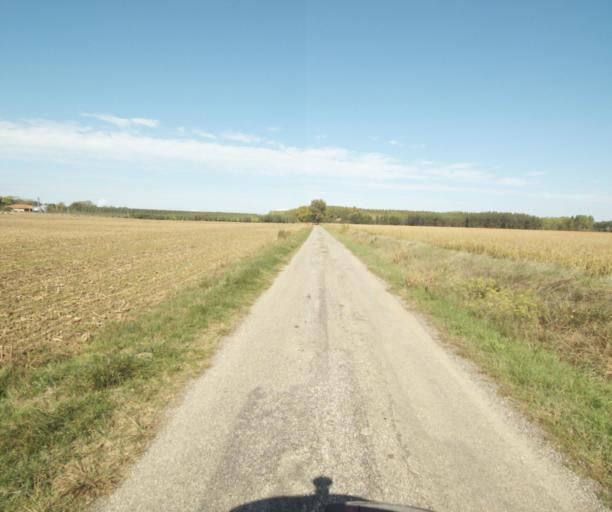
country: FR
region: Midi-Pyrenees
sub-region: Departement du Tarn-et-Garonne
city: Finhan
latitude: 43.8966
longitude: 1.2199
